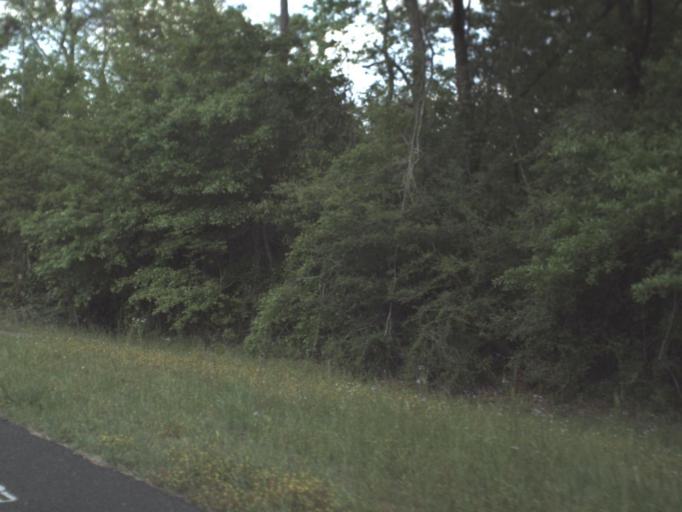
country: US
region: Florida
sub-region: Escambia County
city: Century
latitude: 30.8621
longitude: -87.3233
